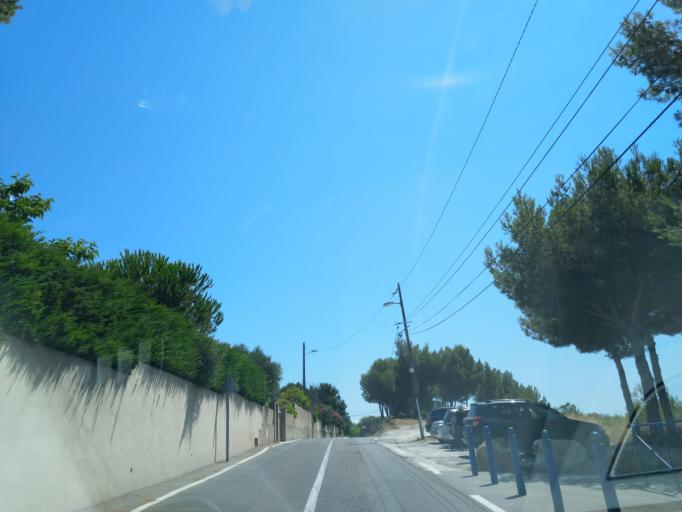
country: FR
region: Provence-Alpes-Cote d'Azur
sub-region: Departement des Bouches-du-Rhone
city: Sausset-les-Pins
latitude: 43.3335
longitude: 5.1103
